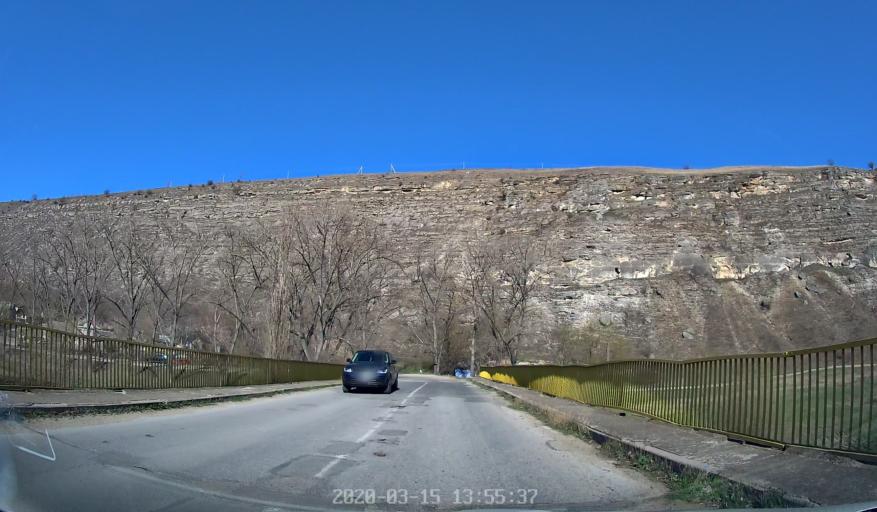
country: MD
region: Telenesti
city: Cocieri
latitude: 47.3086
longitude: 28.9887
